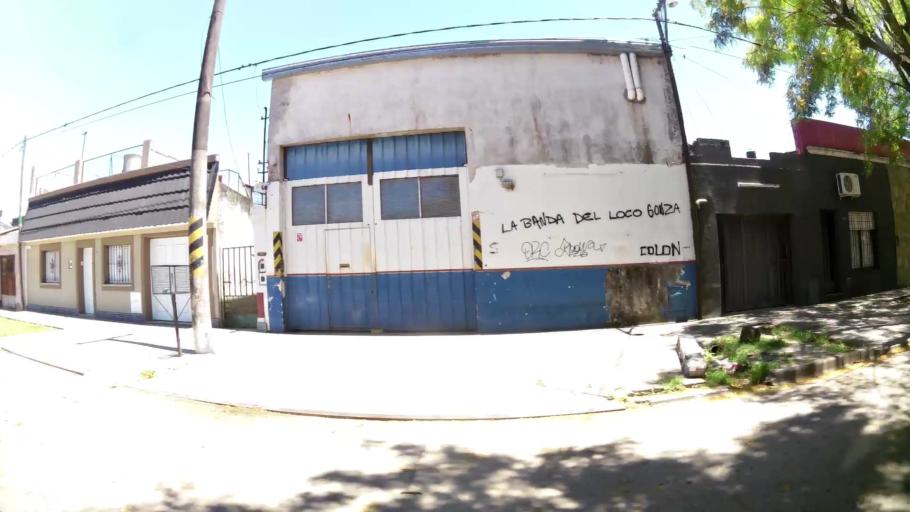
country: AR
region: Santa Fe
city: Santa Fe de la Vera Cruz
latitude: -31.6496
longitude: -60.7269
